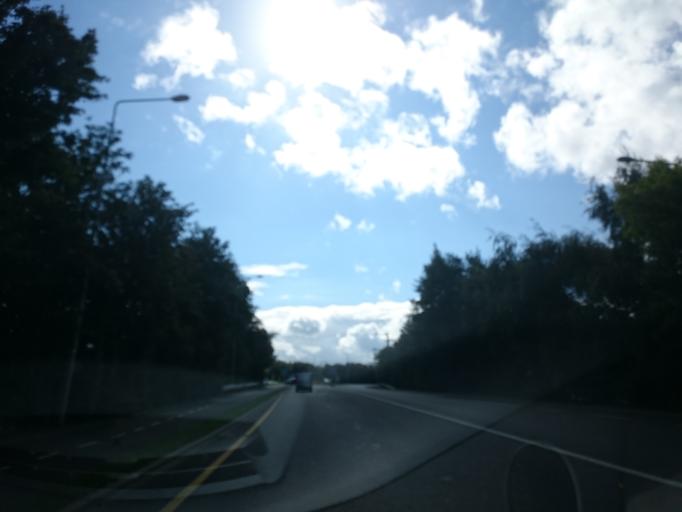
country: IE
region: Leinster
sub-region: Kilkenny
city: Kilkenny
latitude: 52.6387
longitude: -7.2588
